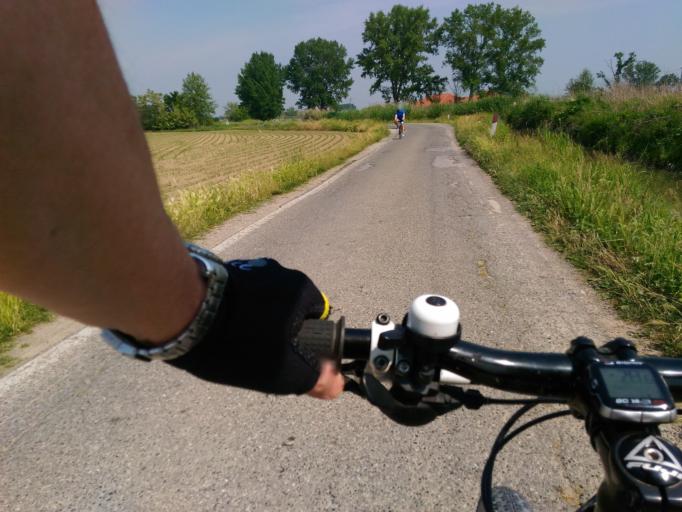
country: IT
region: Lombardy
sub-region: Provincia di Lodi
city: Pieve Fissiraga
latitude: 45.2560
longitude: 9.4678
